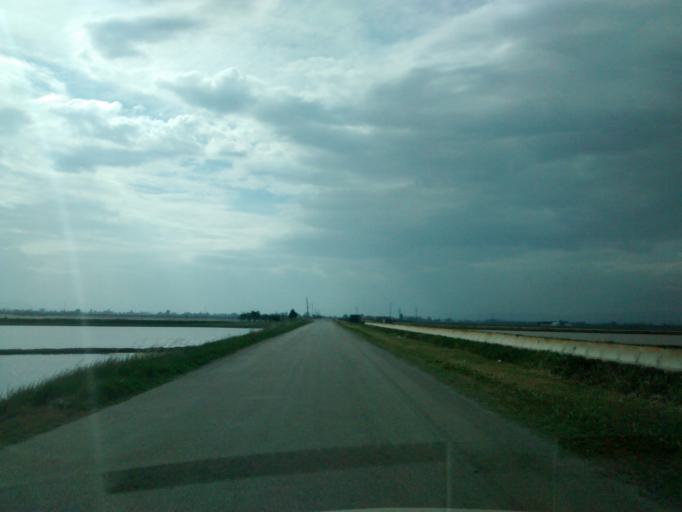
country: ES
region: Catalonia
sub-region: Provincia de Tarragona
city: Deltebre
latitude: 40.6959
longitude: 0.7622
